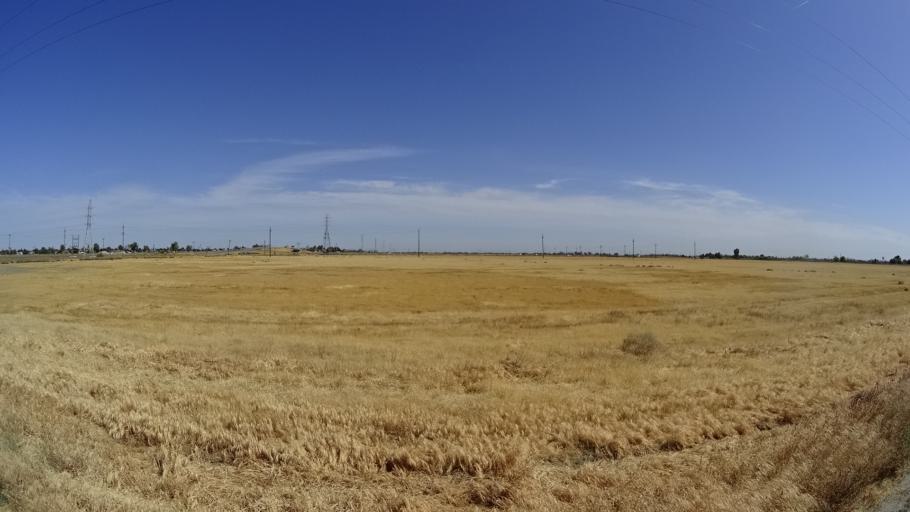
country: US
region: California
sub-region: Kings County
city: Lemoore Station
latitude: 36.2504
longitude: -119.8675
